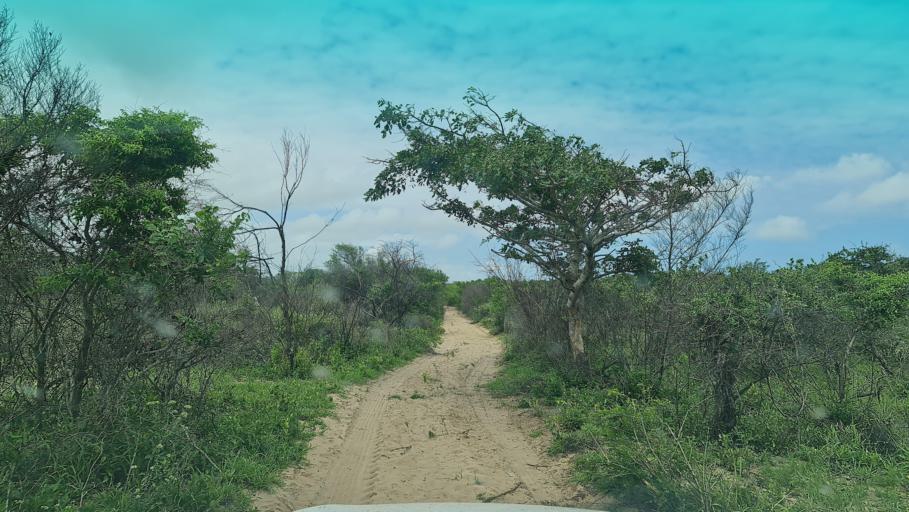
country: MZ
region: Maputo
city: Manhica
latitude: -25.4962
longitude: 32.9027
